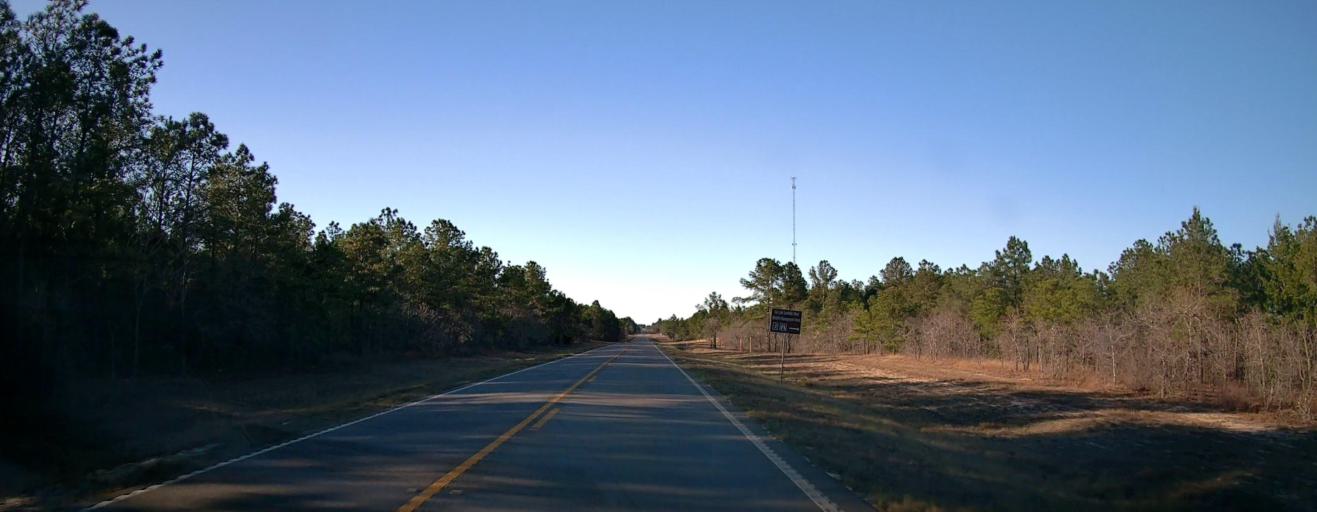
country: US
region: Georgia
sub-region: Talbot County
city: Talbotton
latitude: 32.5663
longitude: -84.4391
